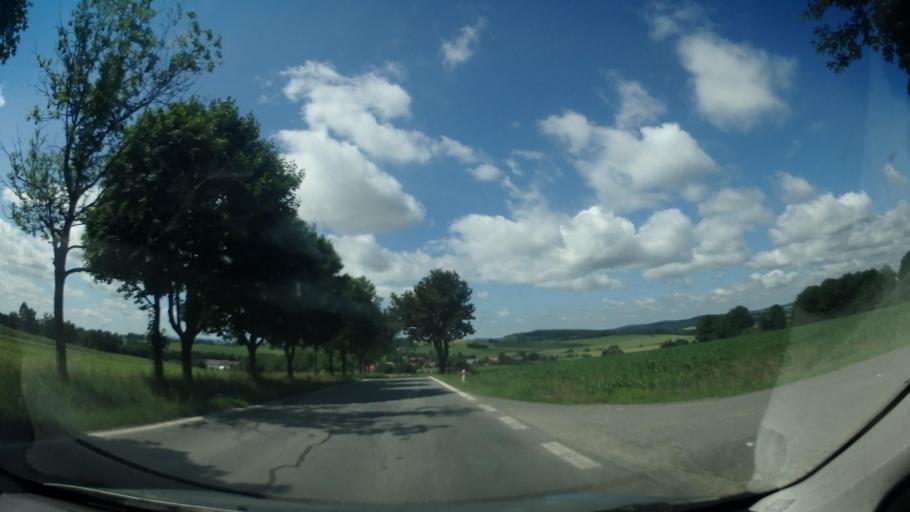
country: CZ
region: Vysocina
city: Zd'ar nad Sazavou Druhy
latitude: 49.5922
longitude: 15.9801
